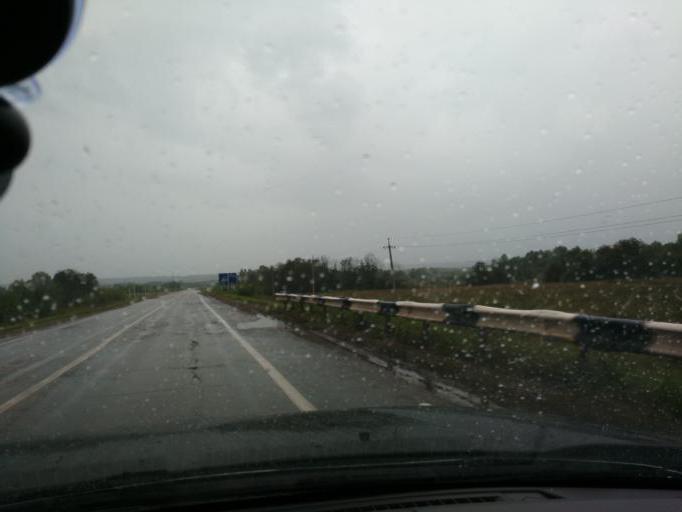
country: RU
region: Perm
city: Barda
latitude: 56.9442
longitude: 55.6210
